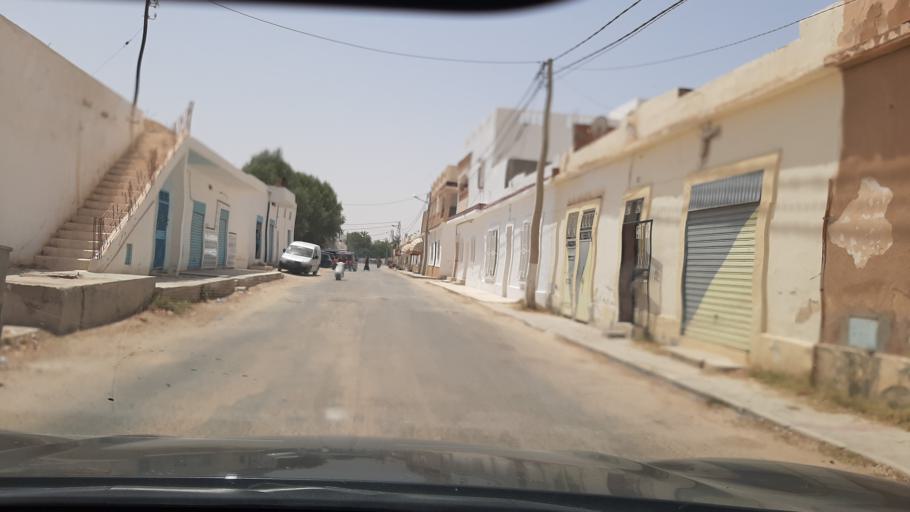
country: TN
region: Qabis
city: Gabes
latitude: 33.6189
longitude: 10.2886
